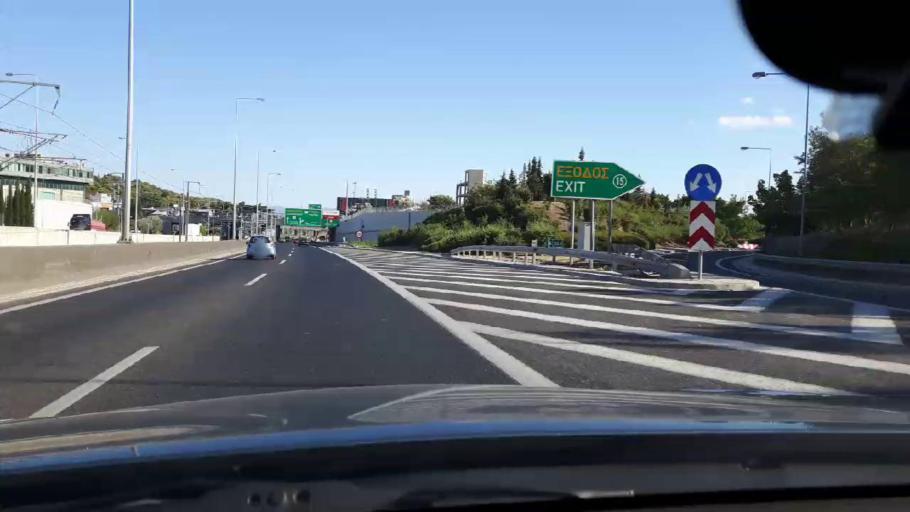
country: GR
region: Attica
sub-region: Nomarchia Anatolikis Attikis
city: Pallini
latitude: 37.9966
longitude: 23.8721
